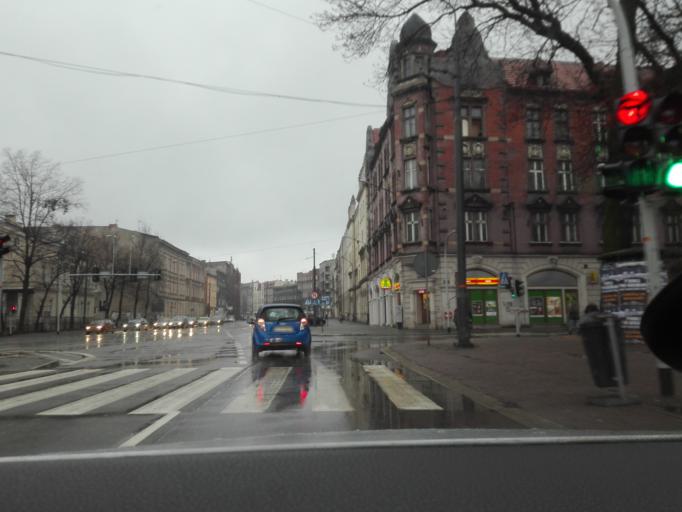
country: PL
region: Silesian Voivodeship
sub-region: Katowice
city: Katowice
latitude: 50.2577
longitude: 19.0310
